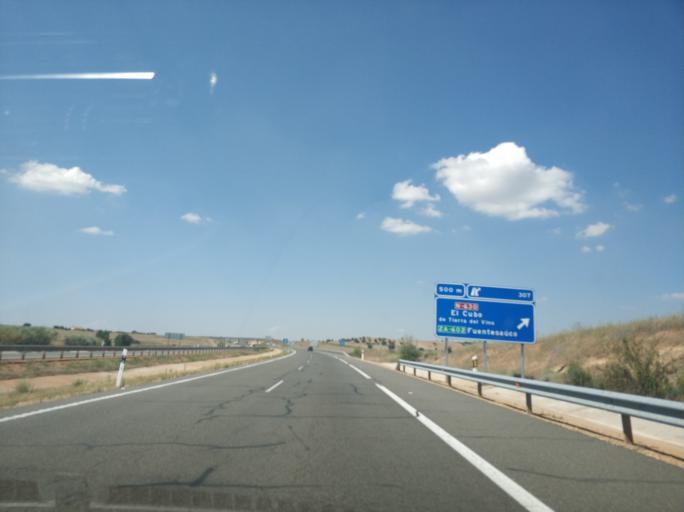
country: ES
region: Castille and Leon
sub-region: Provincia de Zamora
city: Cuelgamures
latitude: 41.2542
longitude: -5.7005
